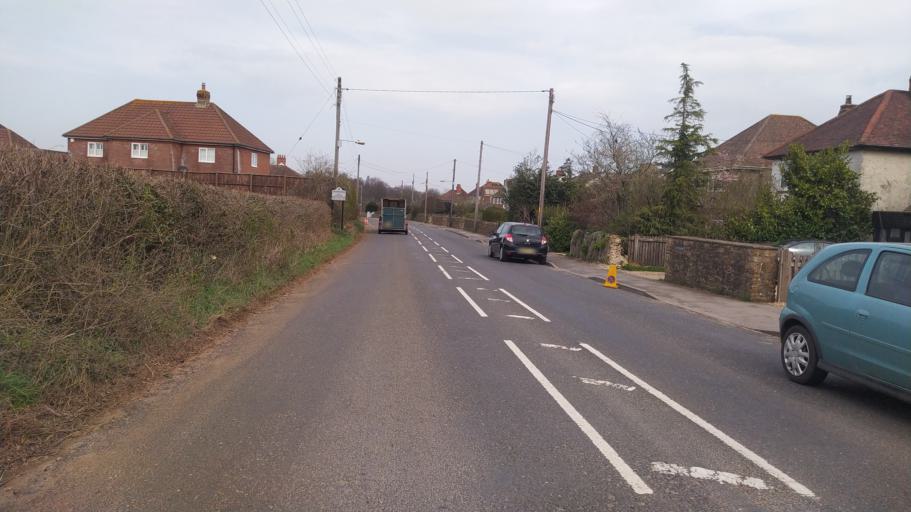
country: GB
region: England
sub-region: Somerset
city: Crewkerne
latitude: 50.8756
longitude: -2.7793
